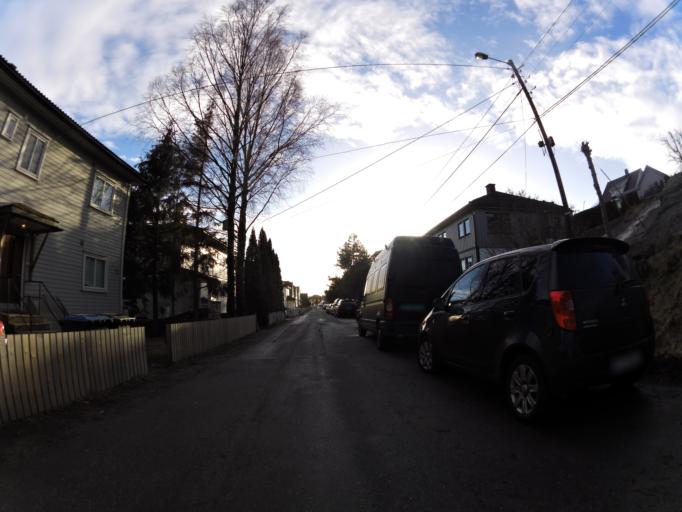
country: NO
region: Ostfold
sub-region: Fredrikstad
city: Fredrikstad
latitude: 59.2215
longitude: 10.9484
